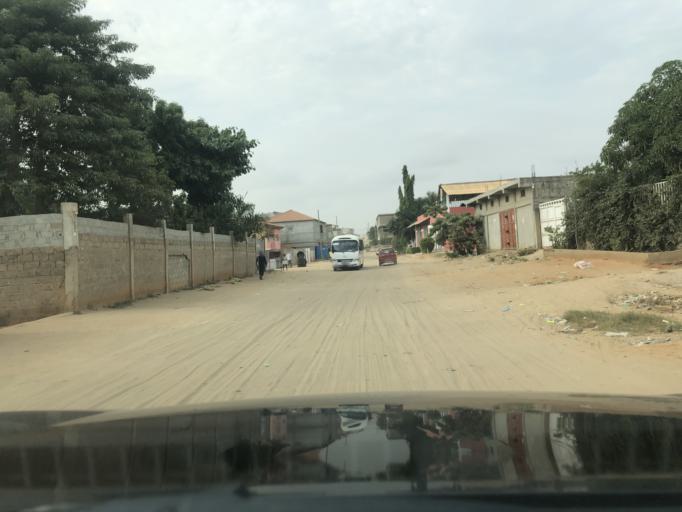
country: AO
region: Luanda
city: Luanda
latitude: -8.9216
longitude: 13.2260
